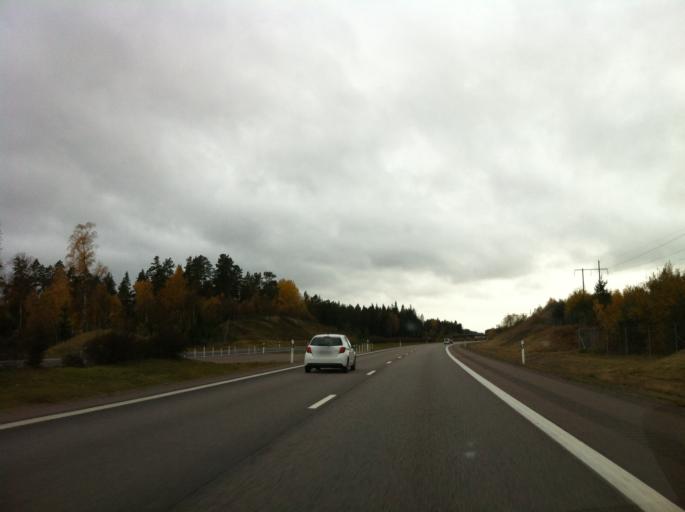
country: SE
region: OEstergoetland
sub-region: Vadstena Kommun
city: Herrestad
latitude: 58.2537
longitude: 14.8158
